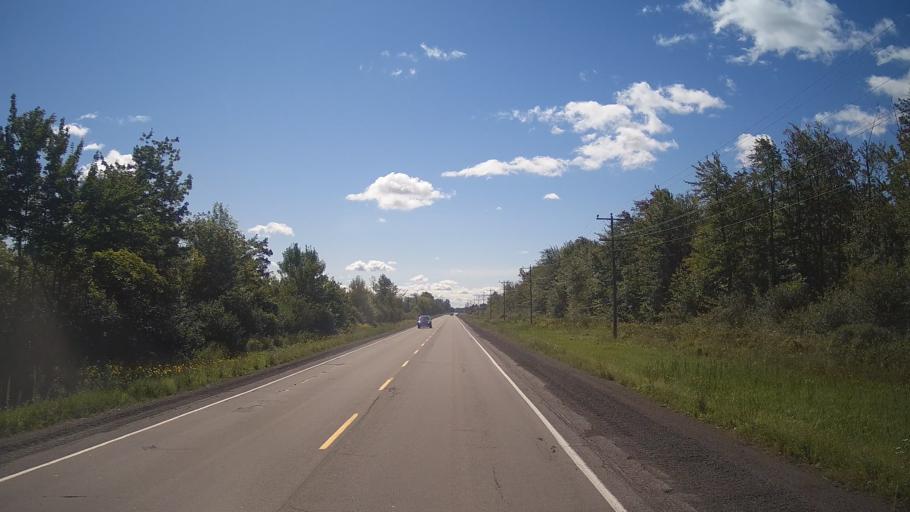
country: US
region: New York
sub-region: St. Lawrence County
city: Norfolk
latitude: 44.9499
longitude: -75.2237
